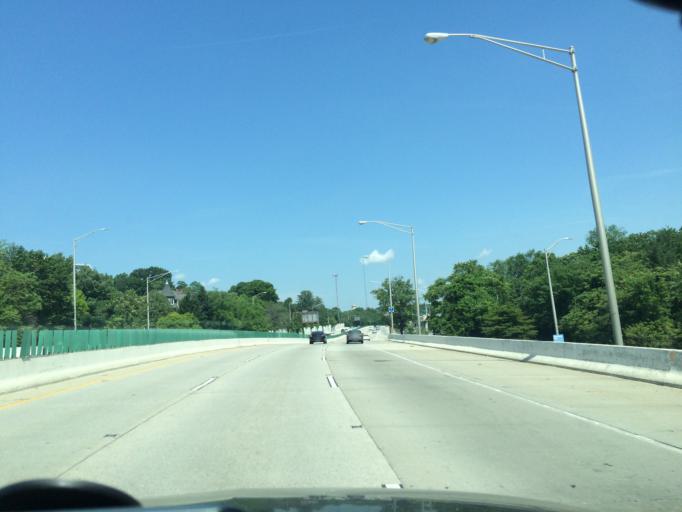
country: US
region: Maryland
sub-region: City of Baltimore
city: Baltimore
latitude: 39.3120
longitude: -76.6248
